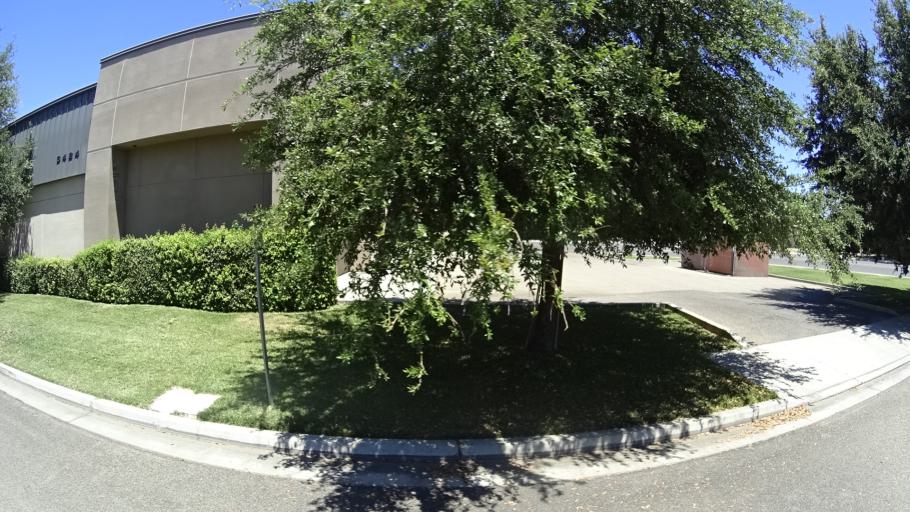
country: US
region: California
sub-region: Fresno County
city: West Park
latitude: 36.8014
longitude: -119.8540
